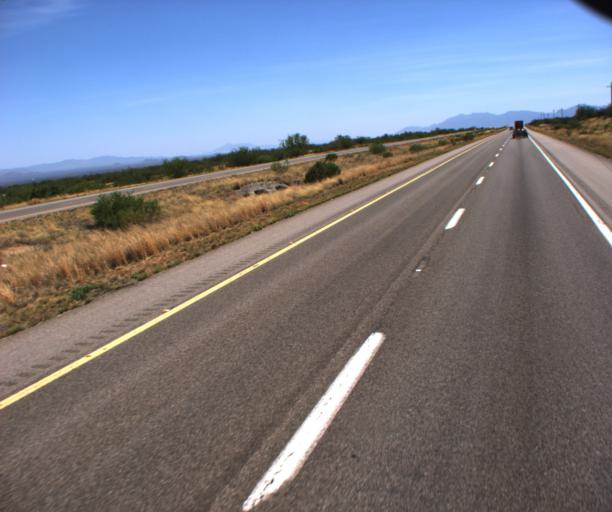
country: US
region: Arizona
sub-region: Cochise County
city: Whetstone
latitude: 31.8667
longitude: -110.3413
